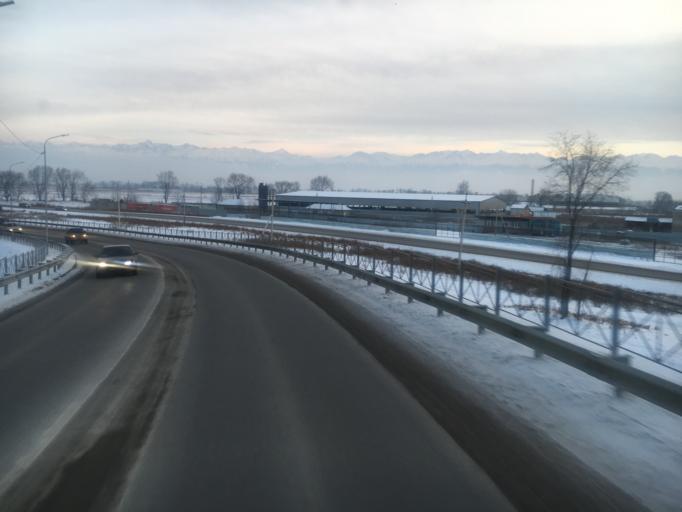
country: KZ
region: Almaty Oblysy
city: Burunday
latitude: 43.3629
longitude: 76.7266
